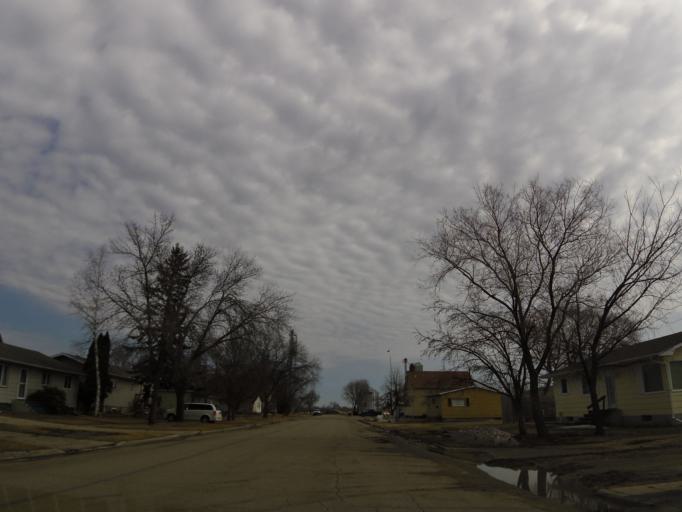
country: US
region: North Dakota
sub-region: Walsh County
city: Grafton
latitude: 48.2926
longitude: -97.3729
